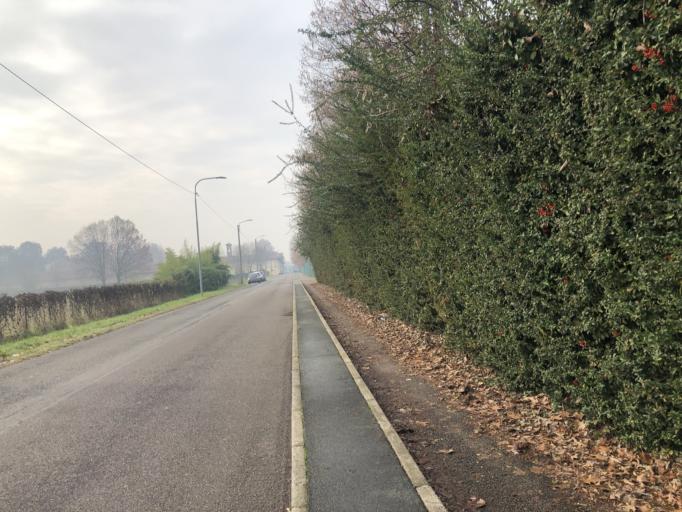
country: IT
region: Lombardy
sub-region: Citta metropolitana di Milano
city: Pregnana Milanese
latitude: 45.5331
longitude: 9.0224
